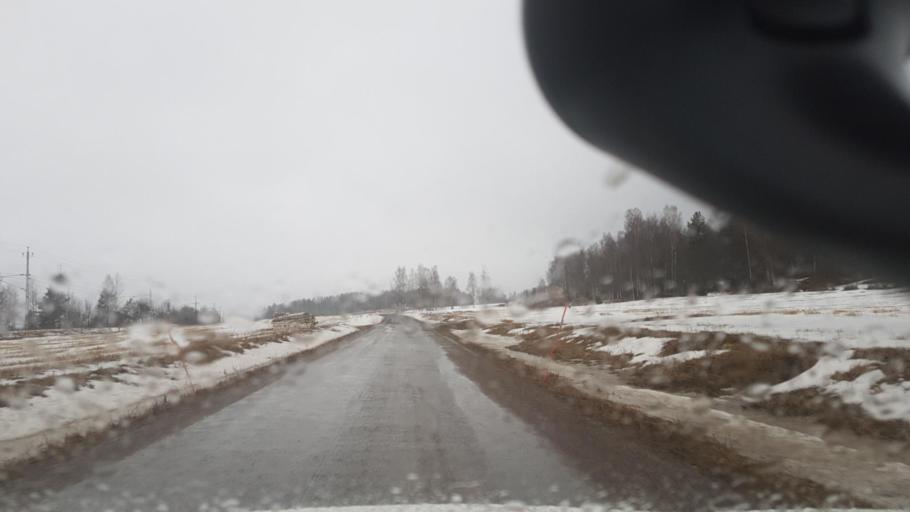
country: SE
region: Vaermland
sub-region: Eda Kommun
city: Amotfors
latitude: 59.8027
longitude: 12.3646
